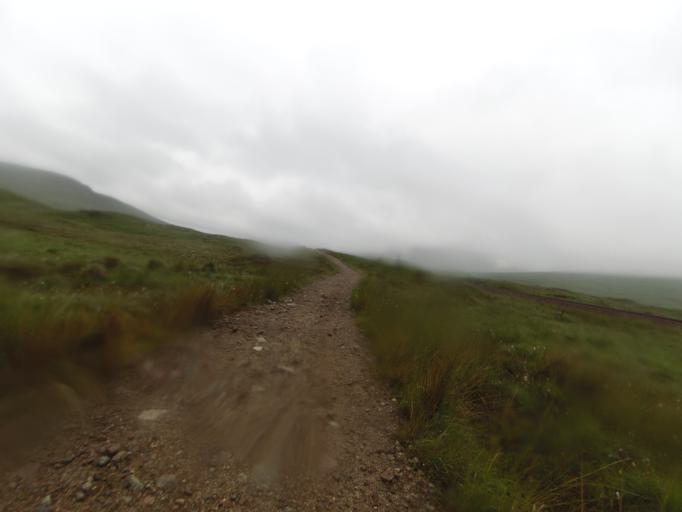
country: GB
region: Scotland
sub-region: Highland
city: Spean Bridge
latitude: 56.7621
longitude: -4.6944
